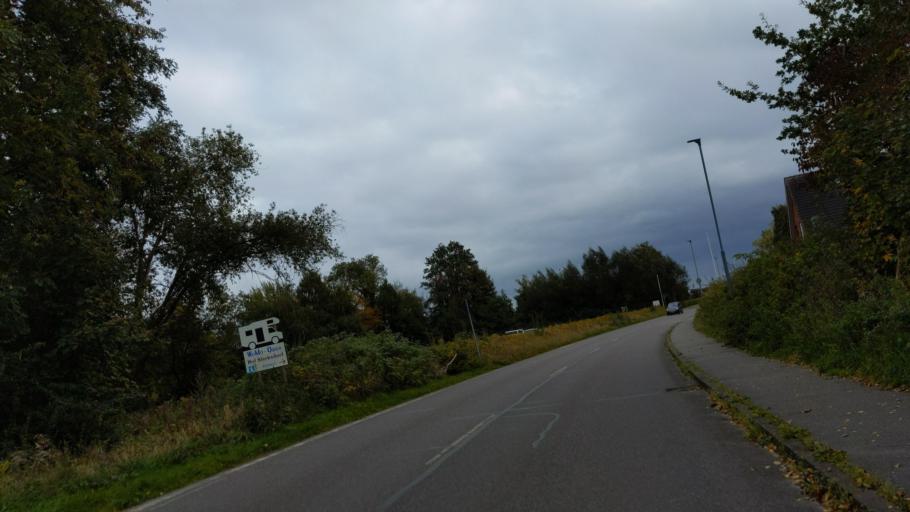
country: DE
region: Schleswig-Holstein
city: Sierksdorf
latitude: 54.0610
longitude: 10.7574
